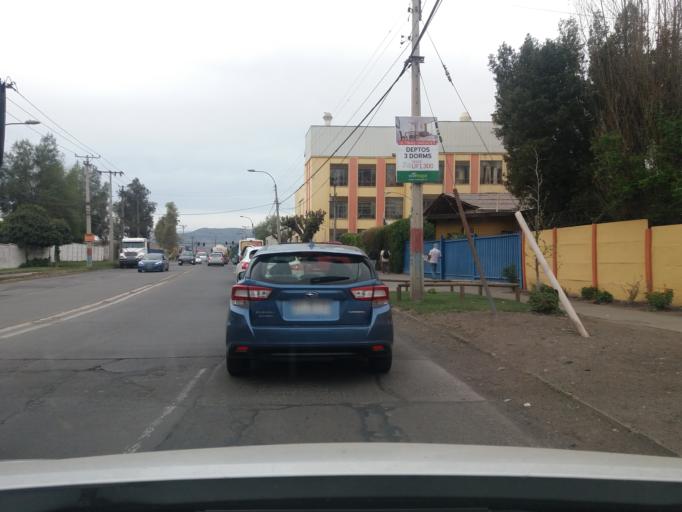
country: CL
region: Valparaiso
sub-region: Provincia de San Felipe
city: San Felipe
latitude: -32.7552
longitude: -70.7319
